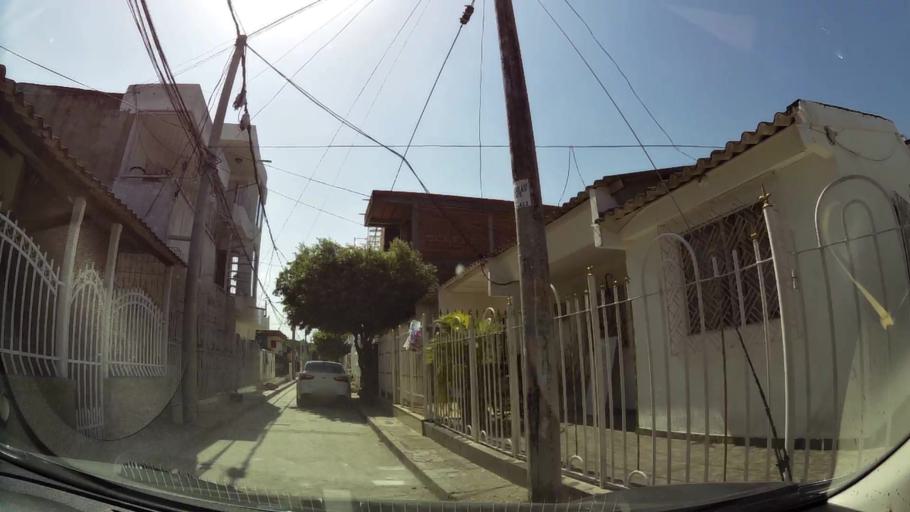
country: CO
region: Bolivar
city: Cartagena
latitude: 10.3788
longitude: -75.4638
